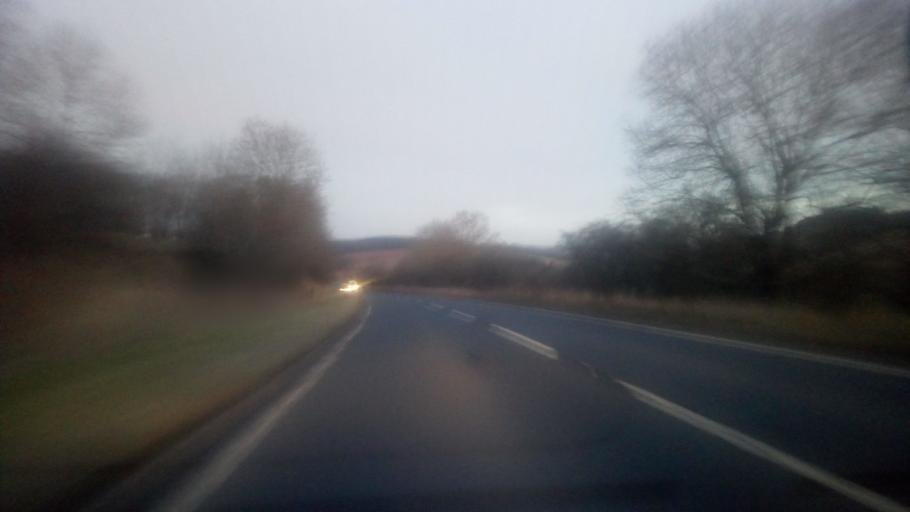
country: GB
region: Scotland
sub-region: The Scottish Borders
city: Lauder
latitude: 55.7663
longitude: -2.7825
